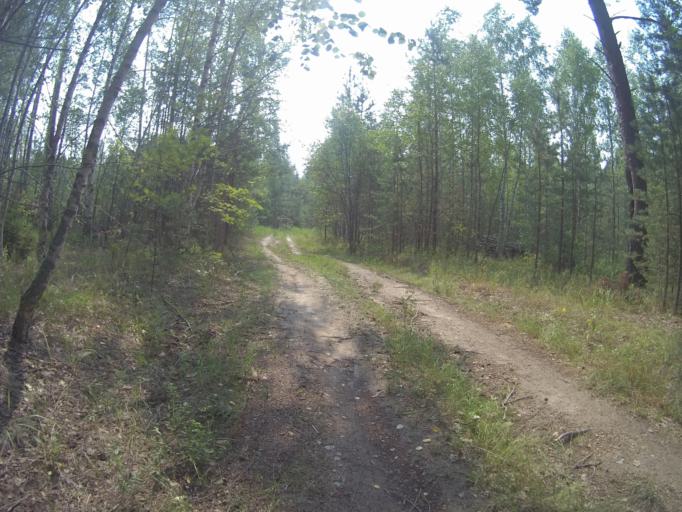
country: RU
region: Vladimir
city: Raduzhnyy
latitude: 55.9813
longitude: 40.2149
